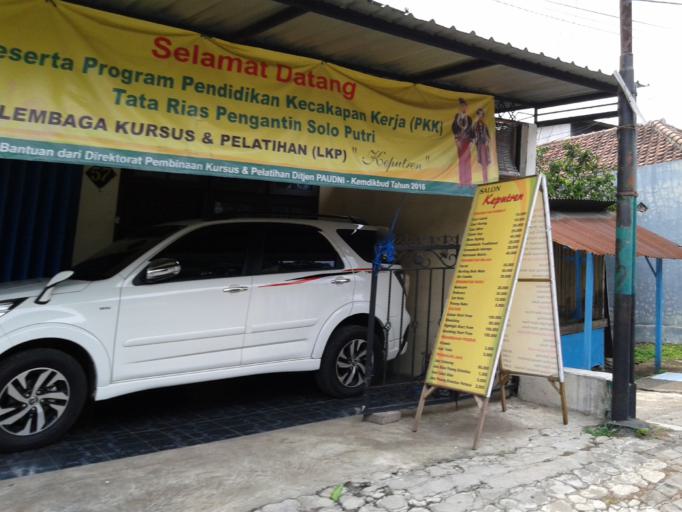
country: ID
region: East Java
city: Singosari
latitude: -7.8952
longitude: 112.6771
